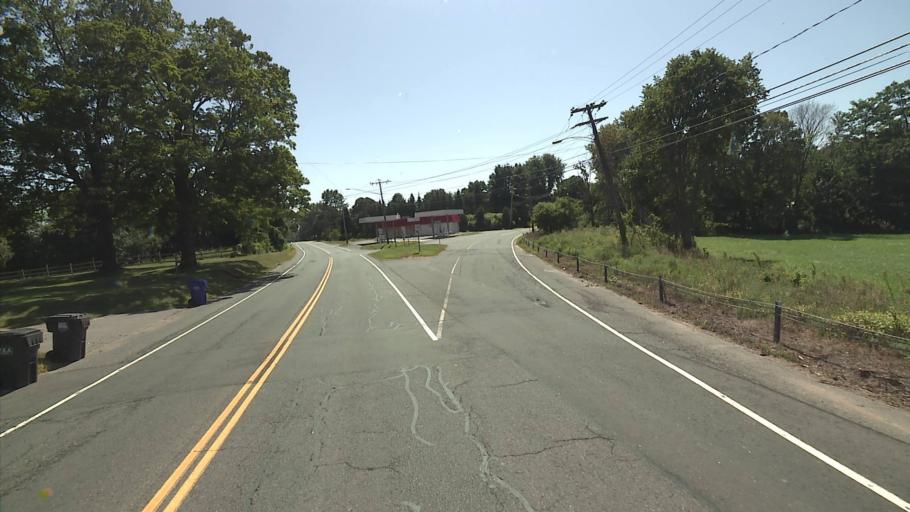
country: US
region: Connecticut
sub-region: Hartford County
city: Thompsonville
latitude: 42.0203
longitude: -72.6169
